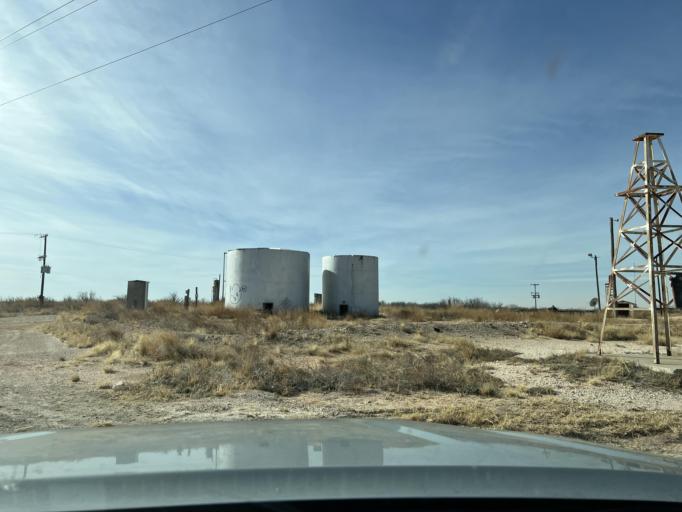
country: US
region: Texas
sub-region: Andrews County
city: Andrews
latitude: 32.3337
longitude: -102.6578
